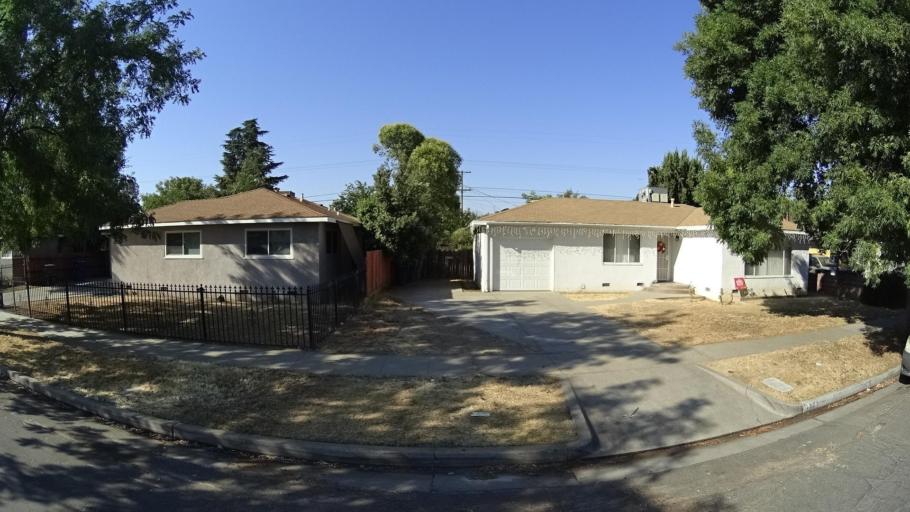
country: US
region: California
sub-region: Fresno County
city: Fresno
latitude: 36.7782
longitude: -119.7699
